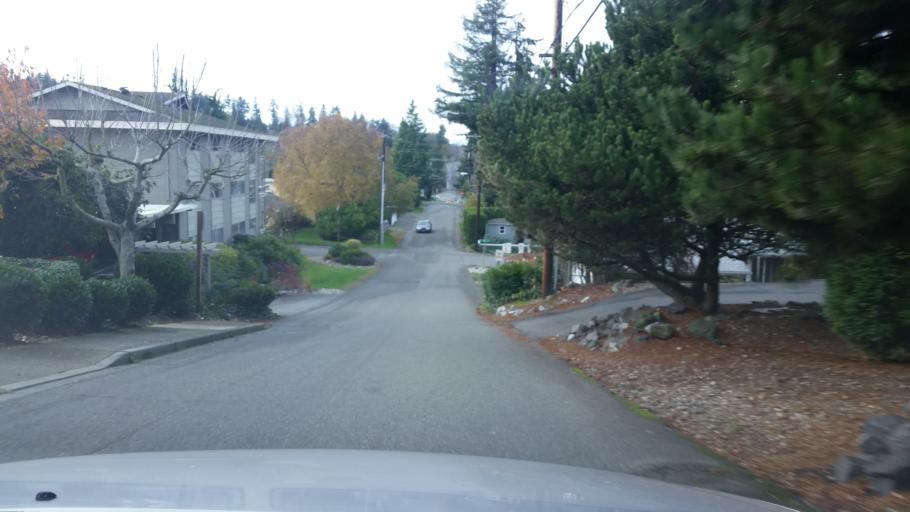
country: US
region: Washington
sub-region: Snohomish County
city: Edmonds
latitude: 47.8032
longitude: -122.3780
